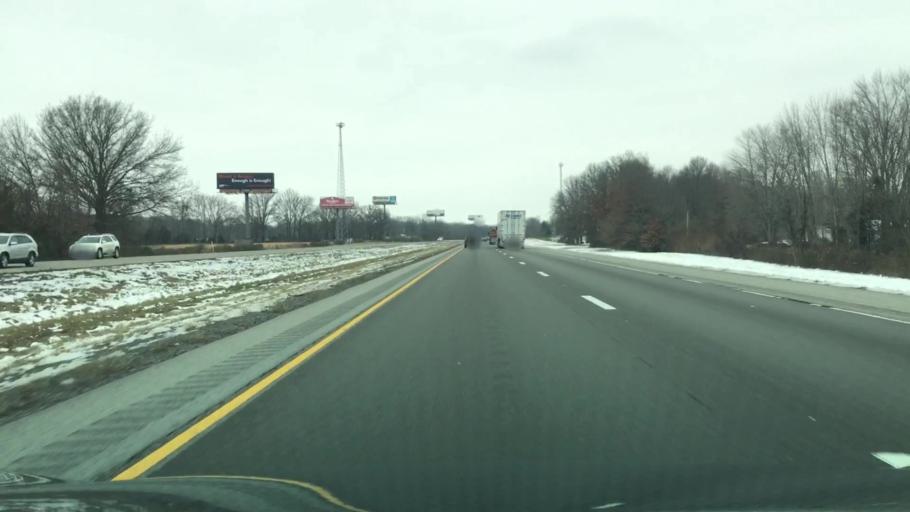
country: US
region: Illinois
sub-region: Jefferson County
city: Ina
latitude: 38.1969
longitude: -88.9074
